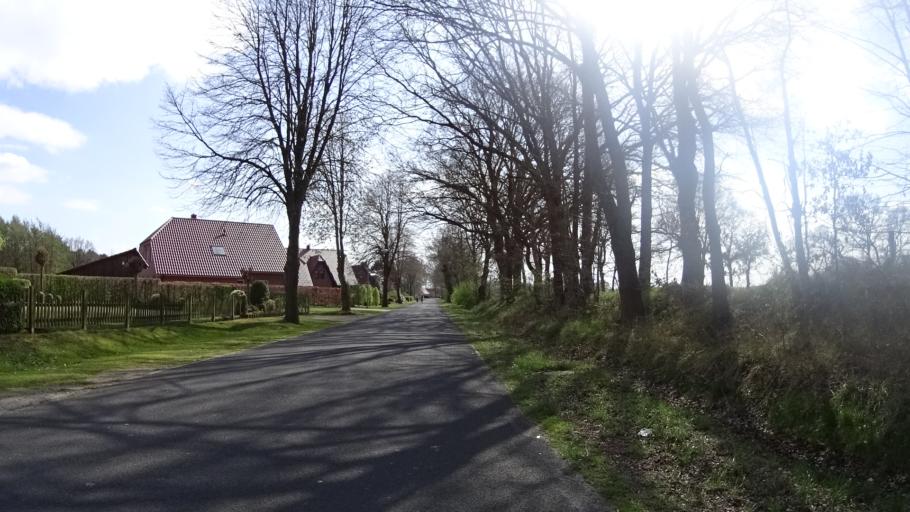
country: DE
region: Lower Saxony
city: Lehe
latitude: 53.0117
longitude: 7.3352
